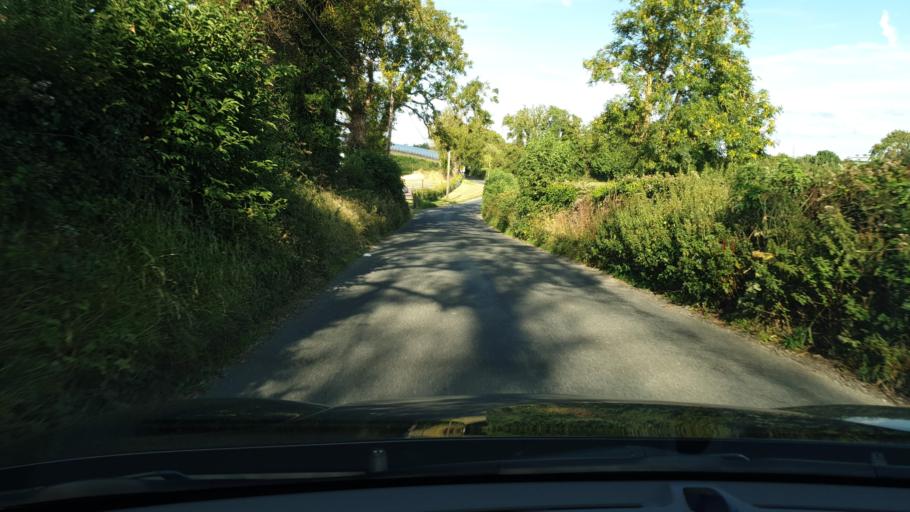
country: IE
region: Leinster
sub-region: An Mhi
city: Stamullin
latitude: 53.6158
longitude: -6.2996
